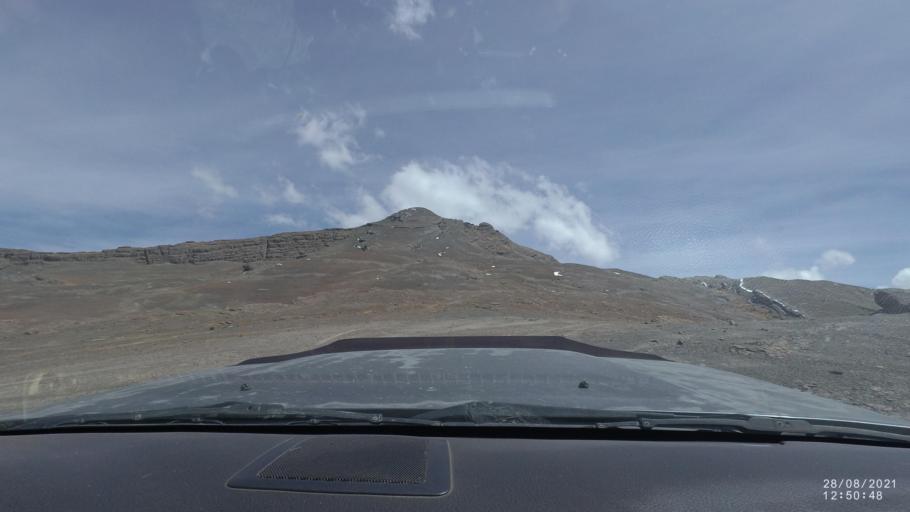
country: BO
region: Cochabamba
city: Sipe Sipe
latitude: -17.2823
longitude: -66.3821
